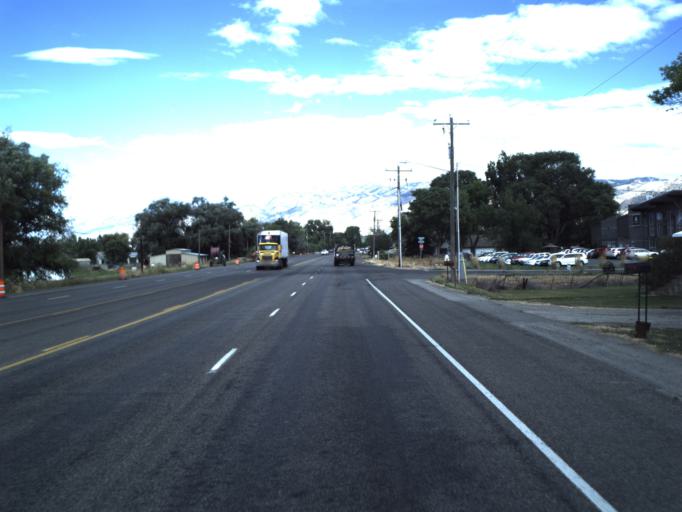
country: US
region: Utah
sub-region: Cache County
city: Nibley
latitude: 41.6906
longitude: -111.8679
